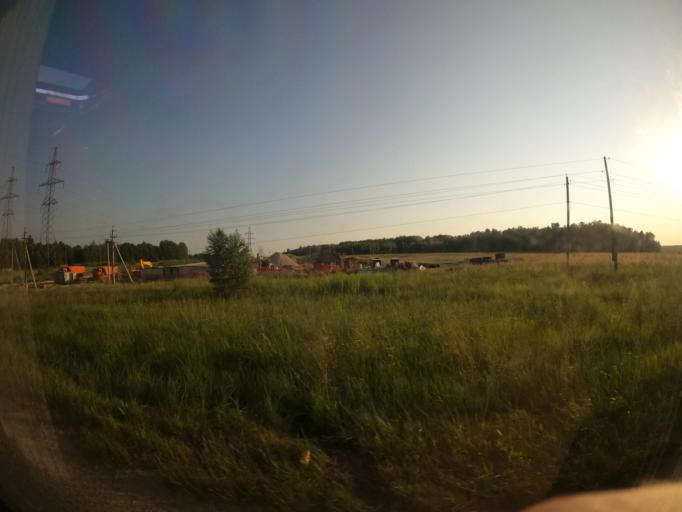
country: RU
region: Moskovskaya
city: Serpukhov
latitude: 54.9493
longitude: 37.3424
